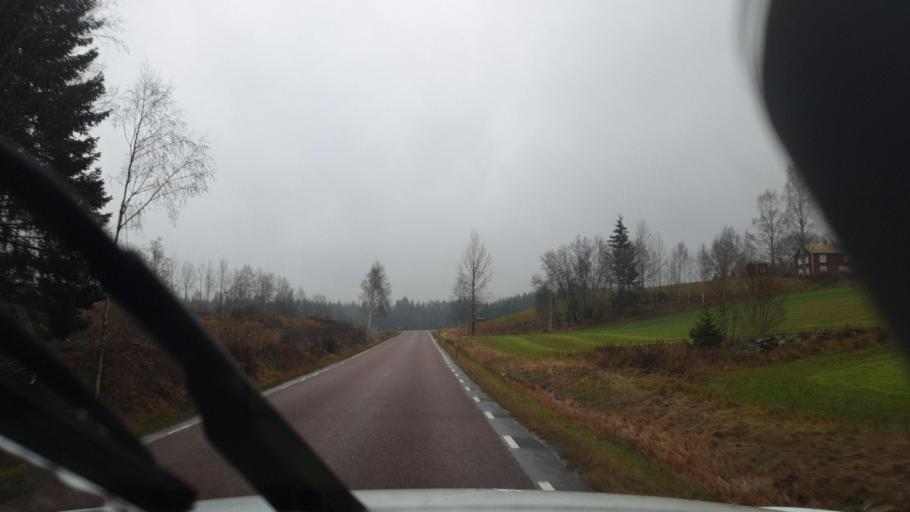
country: SE
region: Vaermland
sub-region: Karlstads Kommun
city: Edsvalla
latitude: 59.5250
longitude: 13.1117
